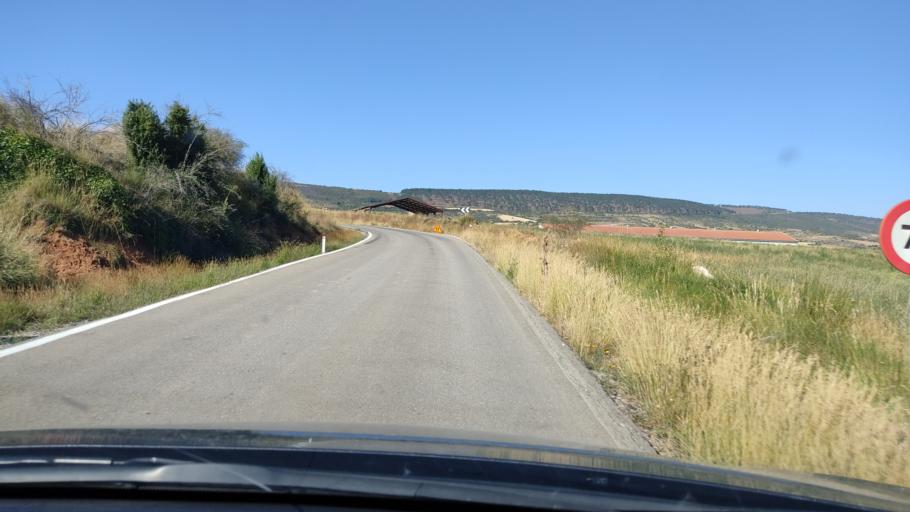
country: ES
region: Aragon
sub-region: Provincia de Teruel
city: Fonfria
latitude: 40.9981
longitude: -1.0802
